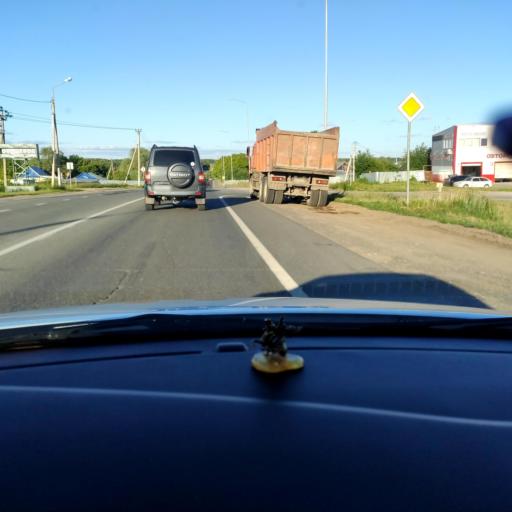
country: RU
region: Tatarstan
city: Aysha
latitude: 55.8711
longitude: 48.6312
